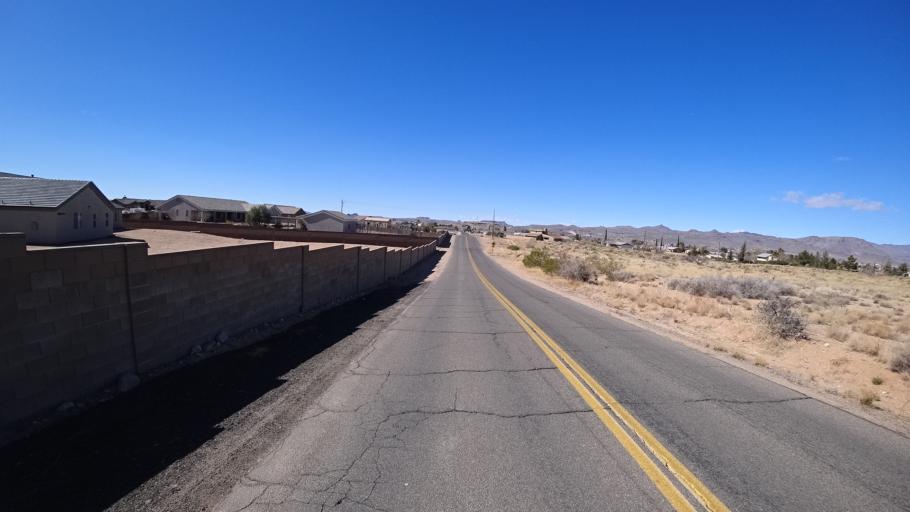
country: US
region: Arizona
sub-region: Mohave County
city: Kingman
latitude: 35.1958
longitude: -114.0010
